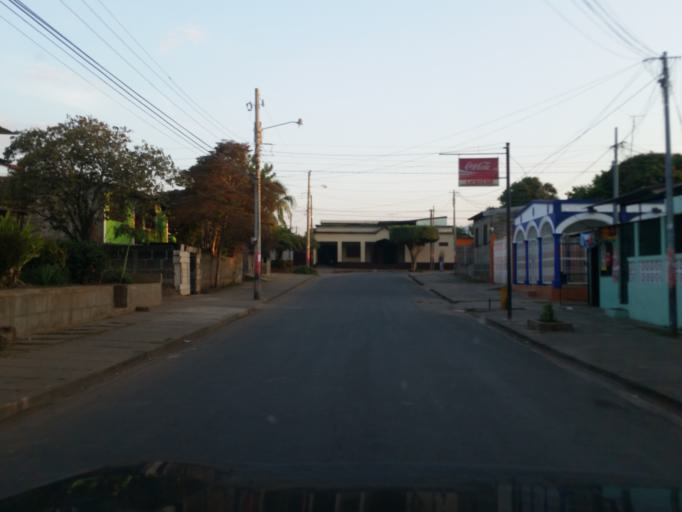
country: NI
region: Granada
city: Granada
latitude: 11.9462
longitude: -85.9466
